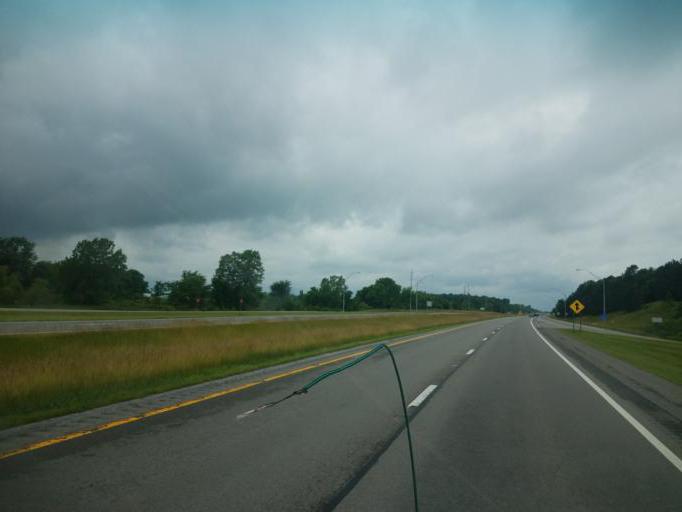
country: US
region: Ohio
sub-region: Logan County
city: Bellefontaine
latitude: 40.4059
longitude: -83.7878
